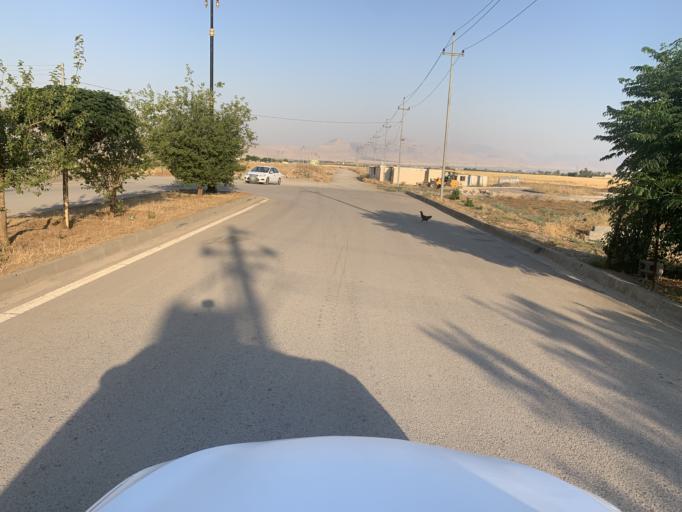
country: IQ
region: As Sulaymaniyah
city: Raniye
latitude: 36.2375
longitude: 44.8812
